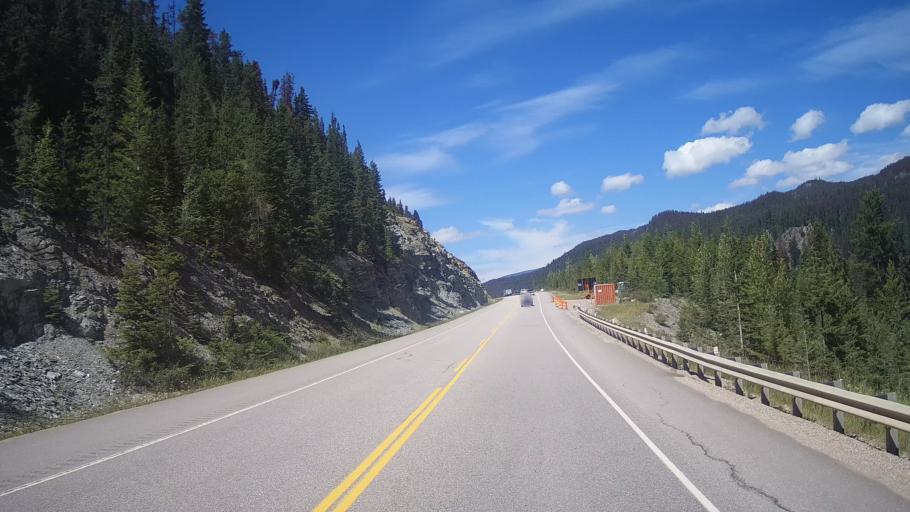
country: CA
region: Alberta
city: Jasper Park Lodge
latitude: 52.8714
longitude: -118.2771
